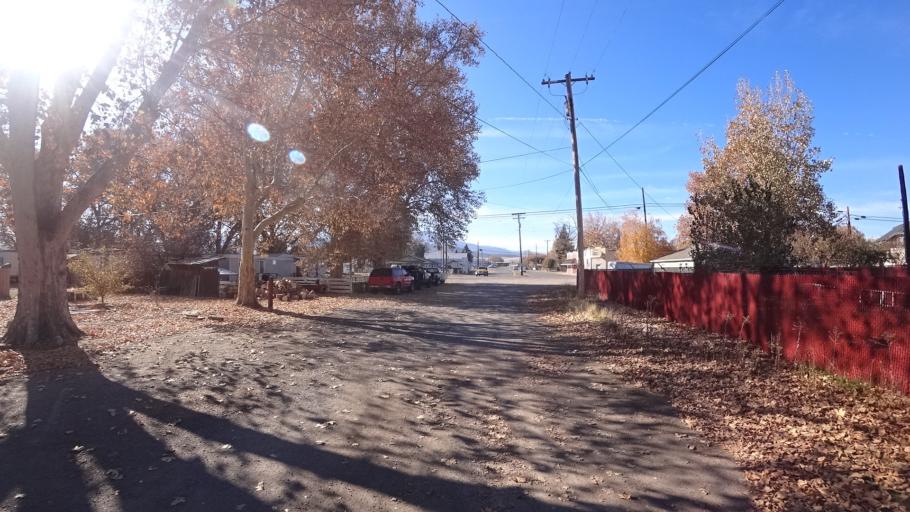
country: US
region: California
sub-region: Siskiyou County
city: Montague
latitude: 41.6454
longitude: -122.5217
